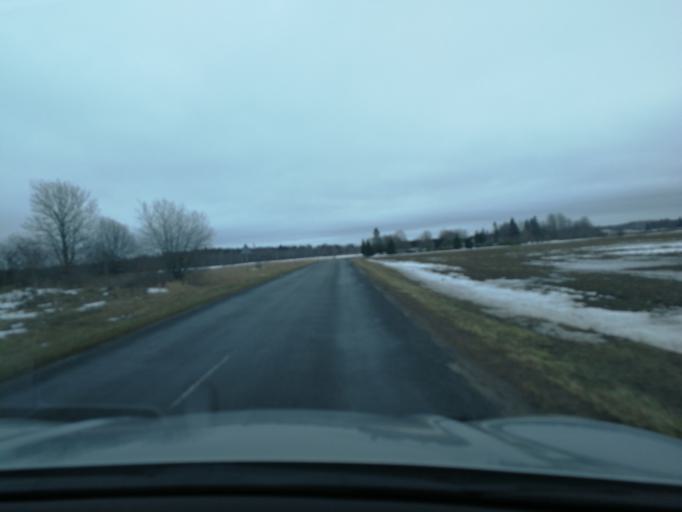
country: EE
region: Harju
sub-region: Kiili vald
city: Kiili
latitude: 59.2897
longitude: 24.8752
